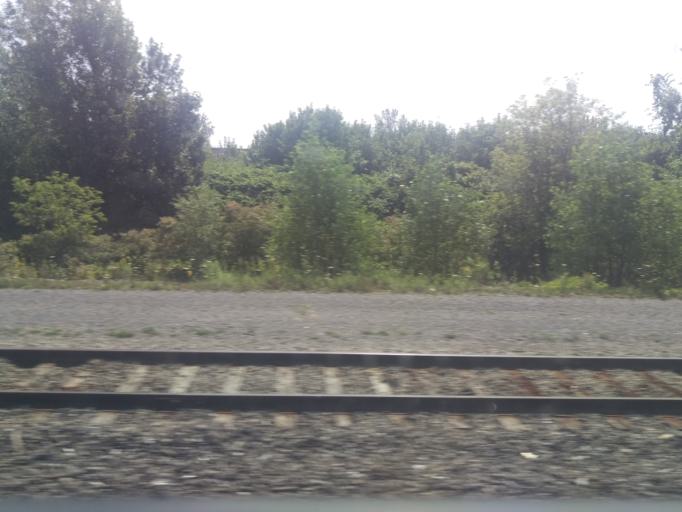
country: CA
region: Ontario
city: Kingston
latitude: 44.2656
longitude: -76.5126
